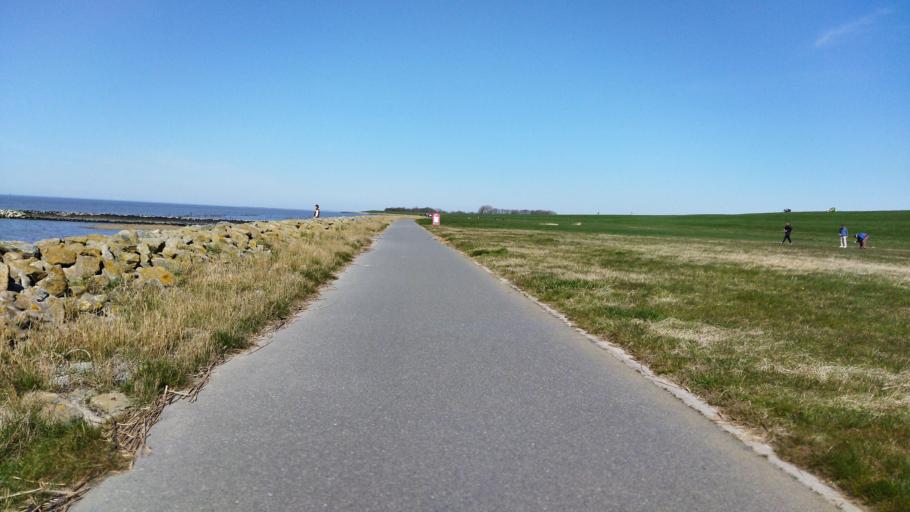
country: DE
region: Lower Saxony
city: Wremen
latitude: 53.6137
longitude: 8.5156
